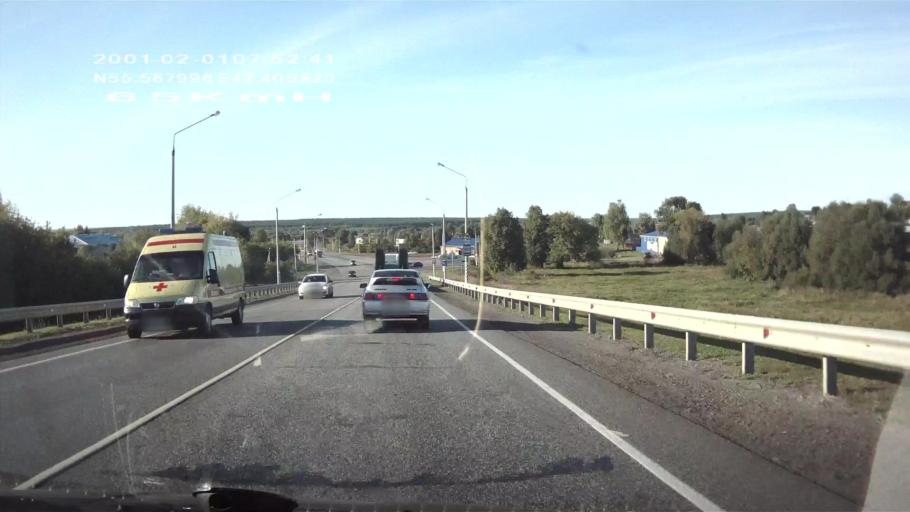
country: RU
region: Chuvashia
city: Shikhazany
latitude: 55.5687
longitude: 47.4047
